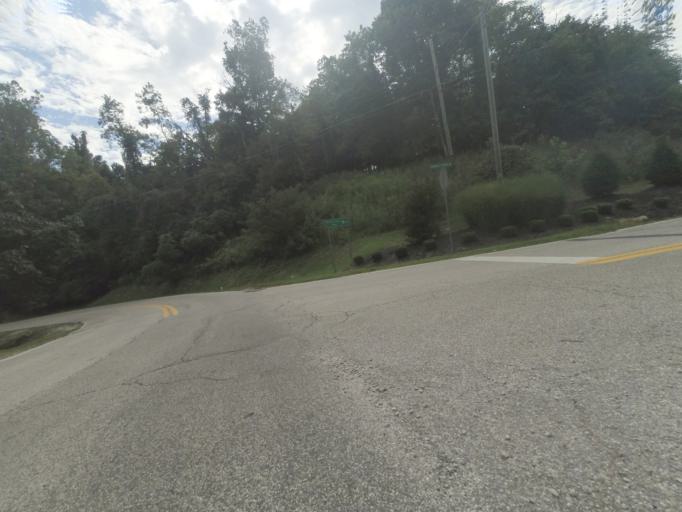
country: US
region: West Virginia
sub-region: Cabell County
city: Huntington
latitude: 38.3923
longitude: -82.4603
